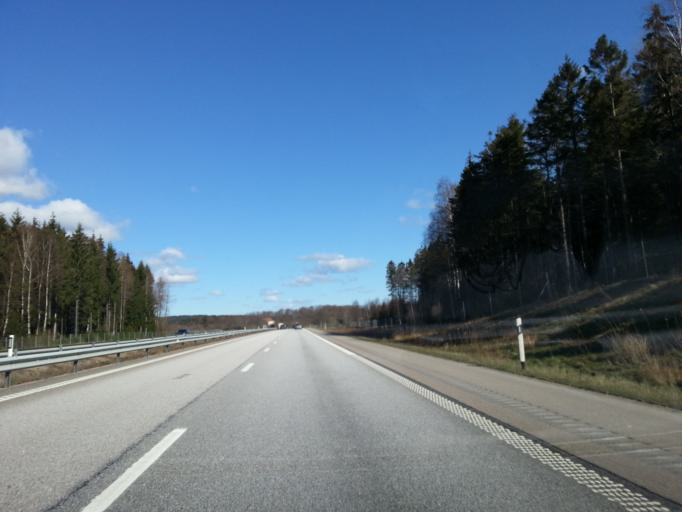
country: SE
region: Vaestra Goetaland
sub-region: Uddevalla Kommun
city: Uddevalla
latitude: 58.3094
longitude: 11.8594
